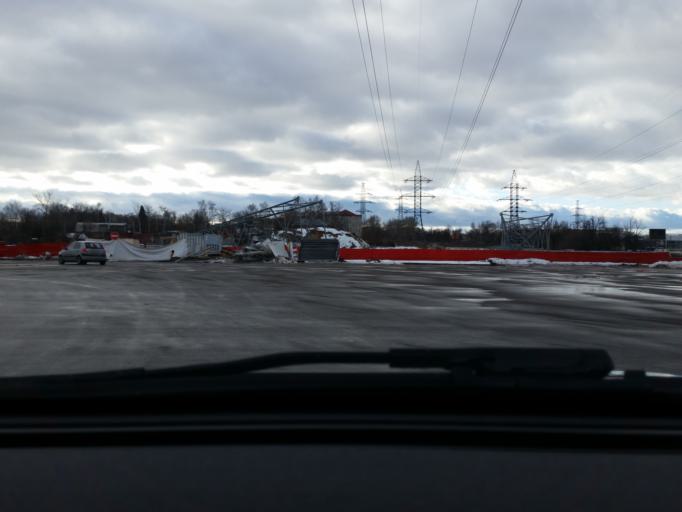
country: RU
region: Moskovskaya
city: Shcherbinka
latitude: 55.4926
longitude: 37.5712
